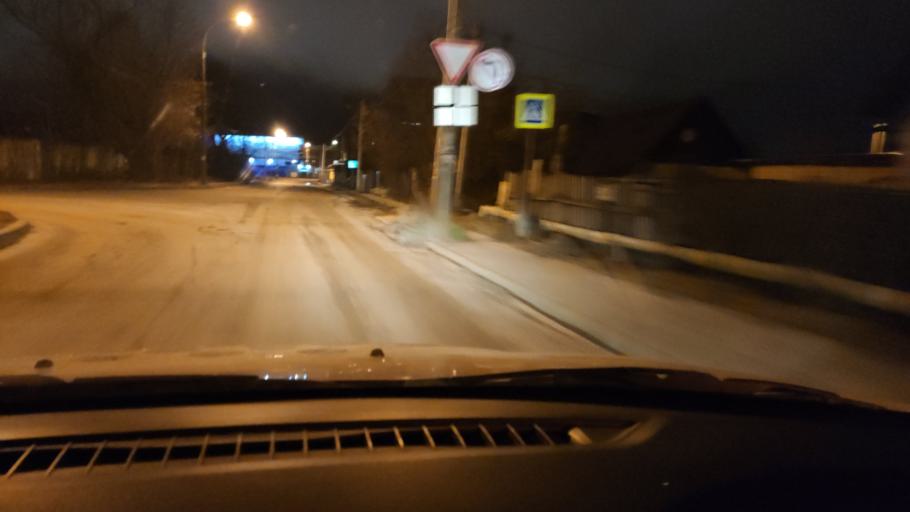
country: RU
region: Perm
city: Perm
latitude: 57.9750
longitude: 56.2677
